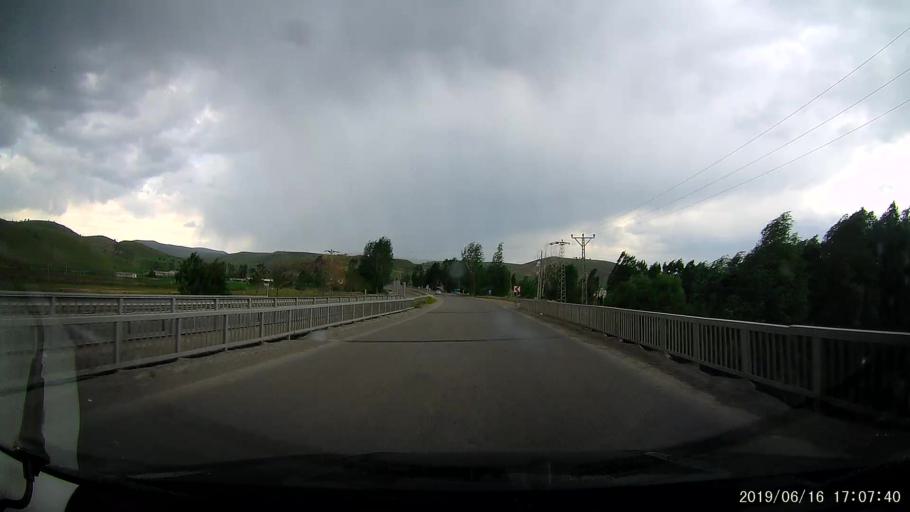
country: TR
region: Erzurum
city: Askale
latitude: 39.9170
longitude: 40.6716
